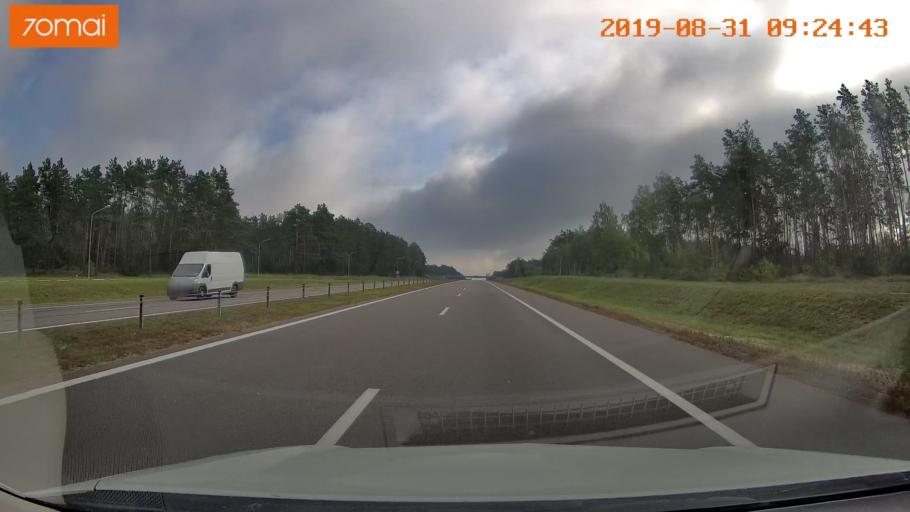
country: BY
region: Minsk
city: Byerazino
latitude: 53.8210
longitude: 28.9572
